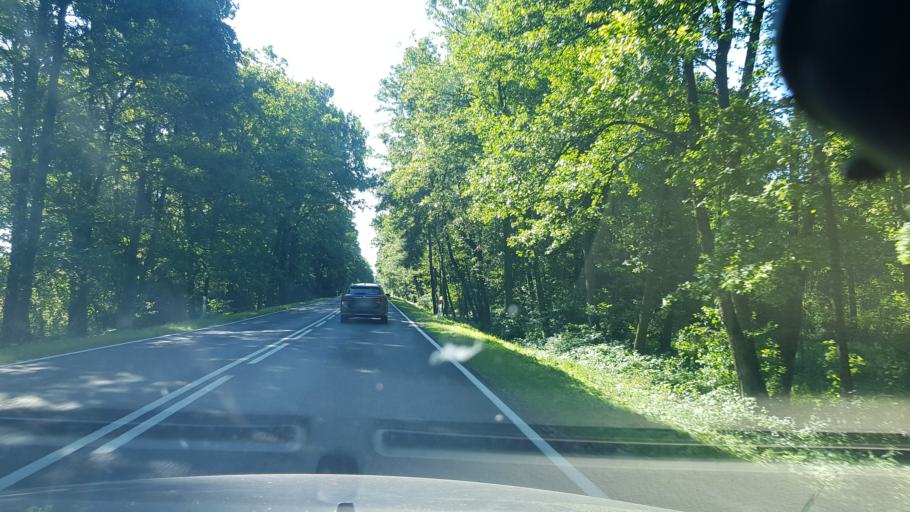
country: PL
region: Masovian Voivodeship
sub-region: Powiat wyszkowski
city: Wyszkow
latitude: 52.5857
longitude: 21.5224
